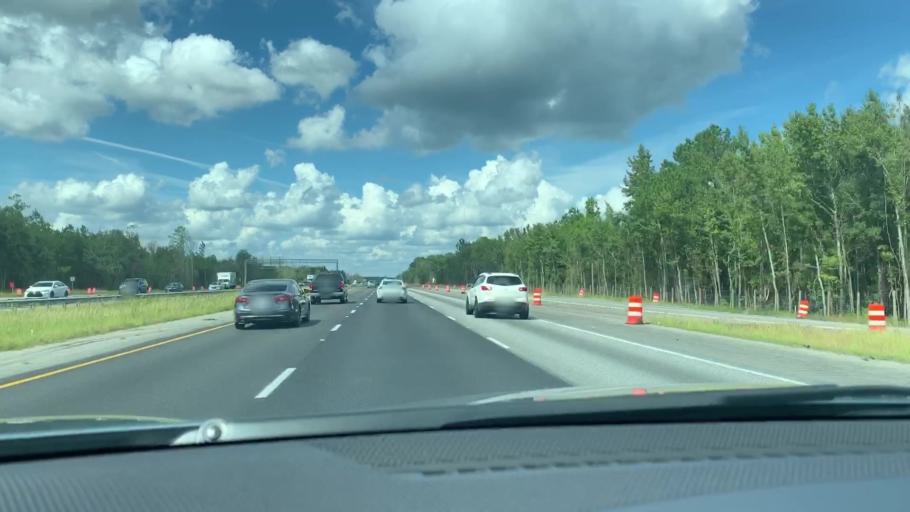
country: US
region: Georgia
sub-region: Camden County
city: Kingsland
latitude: 30.8497
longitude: -81.6735
